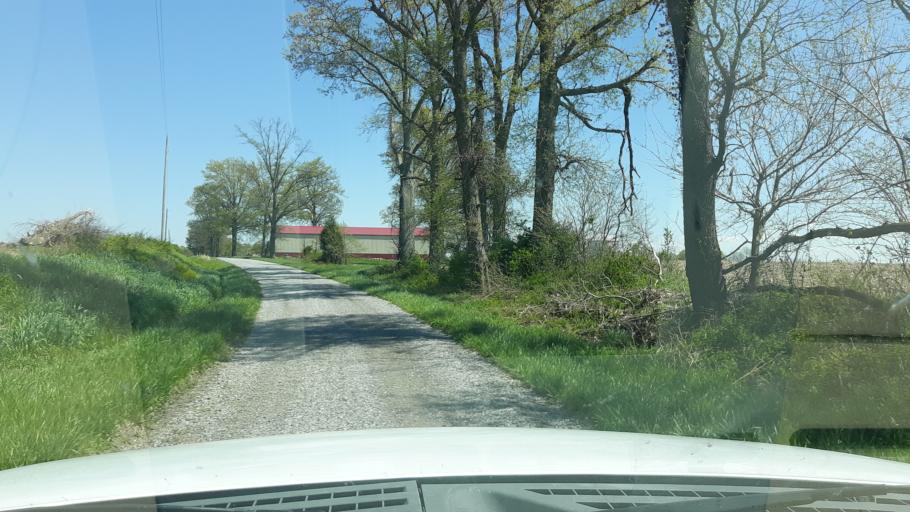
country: US
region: Illinois
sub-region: Saline County
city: Harrisburg
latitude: 37.8887
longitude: -88.6756
